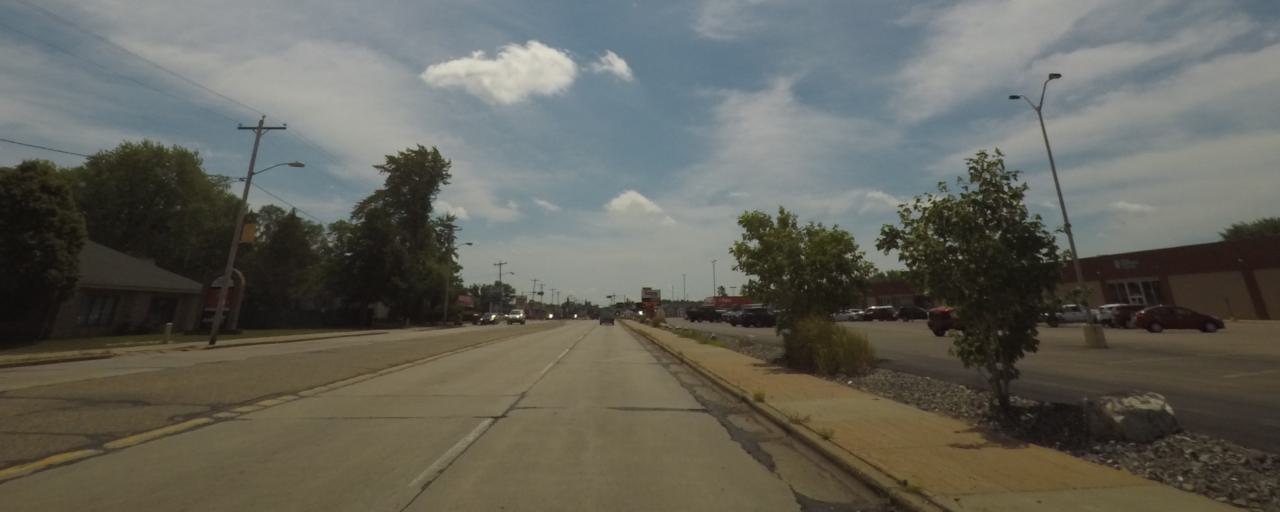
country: US
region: Wisconsin
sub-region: Portage County
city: Whiting
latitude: 44.5040
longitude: -89.5665
